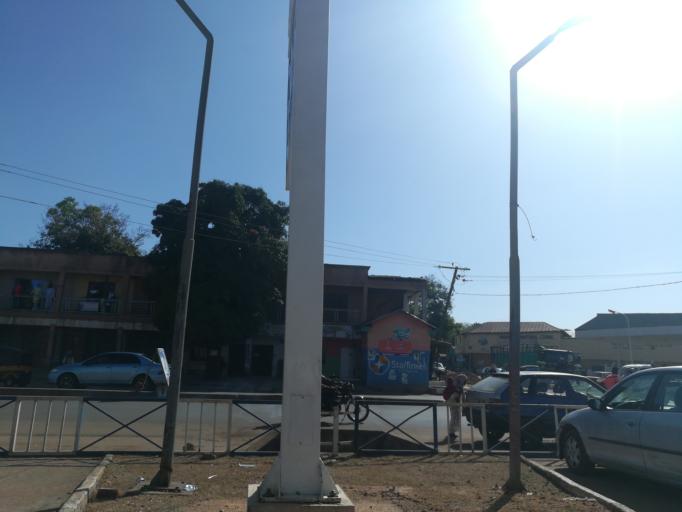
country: NG
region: Plateau
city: Jos
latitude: 9.9388
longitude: 8.8942
